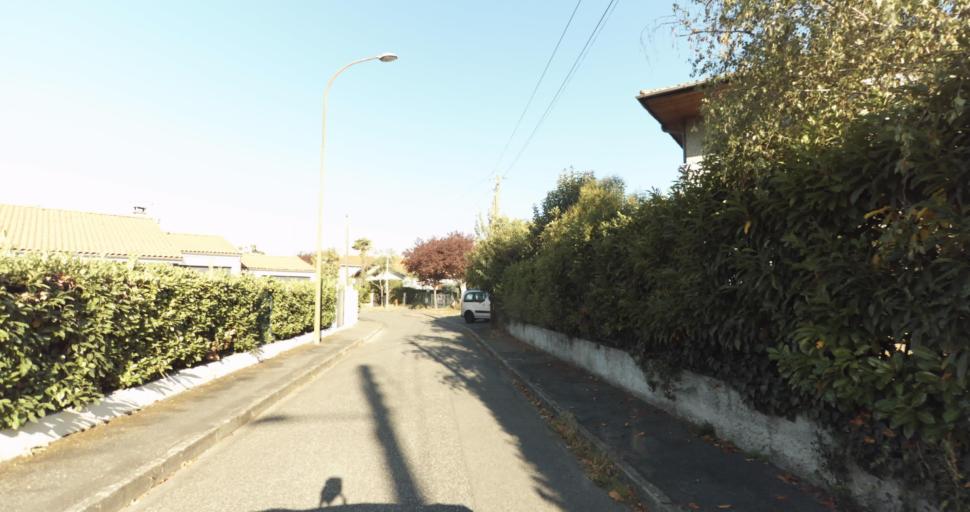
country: FR
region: Midi-Pyrenees
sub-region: Departement de la Haute-Garonne
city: L'Union
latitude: 43.6538
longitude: 1.4723
